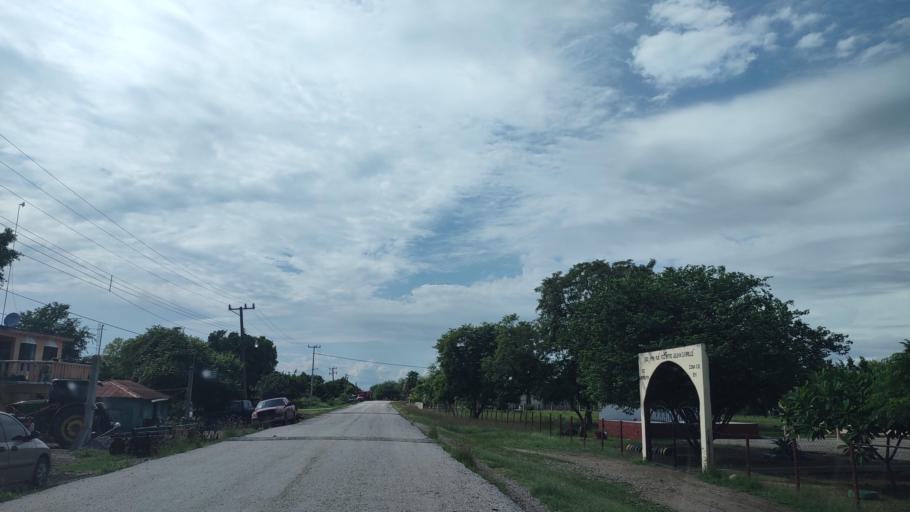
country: MX
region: Veracruz
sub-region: Panuco
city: Oviedo
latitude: 22.0031
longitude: -98.4593
